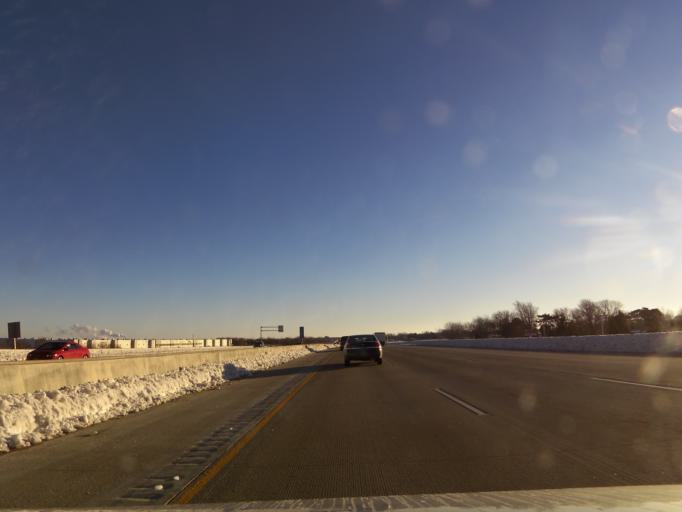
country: US
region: Wisconsin
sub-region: Kenosha County
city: Somers
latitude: 42.6140
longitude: -87.9524
